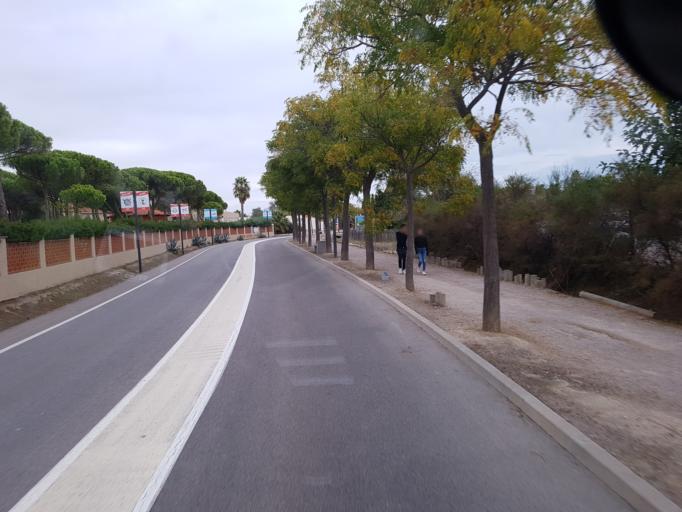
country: FR
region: Languedoc-Roussillon
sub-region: Departement des Pyrenees-Orientales
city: Le Barcares
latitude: 42.7664
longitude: 3.0279
